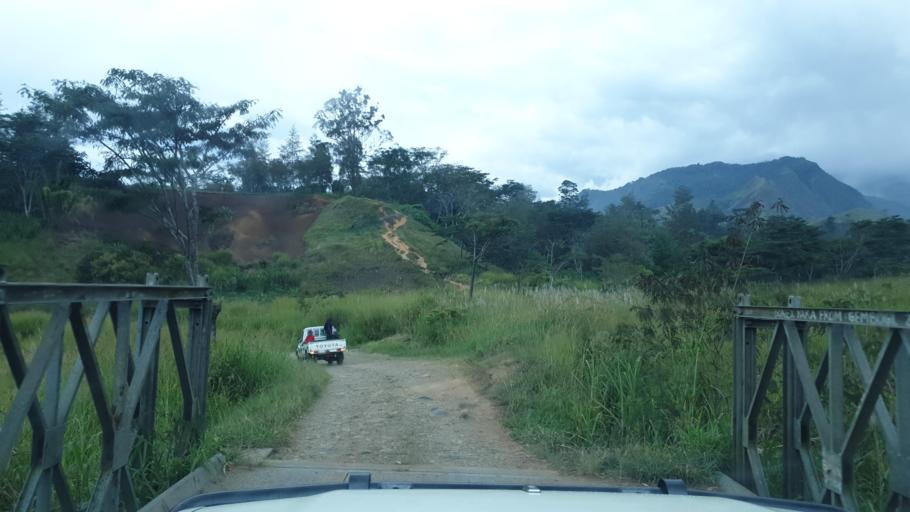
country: PG
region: Eastern Highlands
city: Goroka
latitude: -5.9865
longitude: 145.2823
